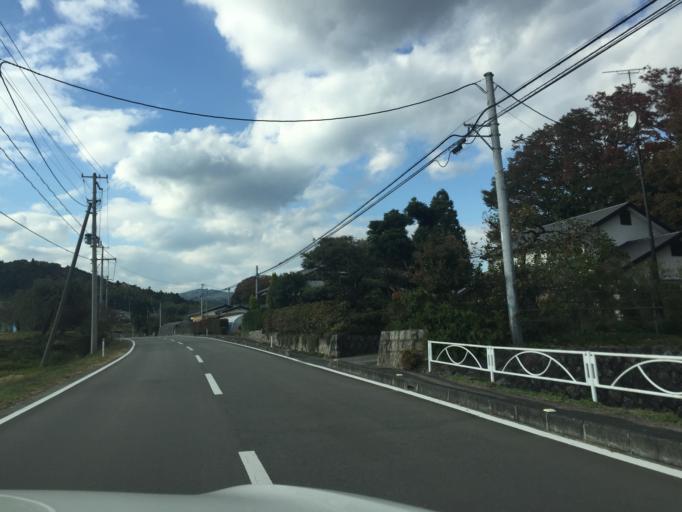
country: JP
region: Fukushima
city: Iwaki
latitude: 37.1366
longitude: 140.8457
